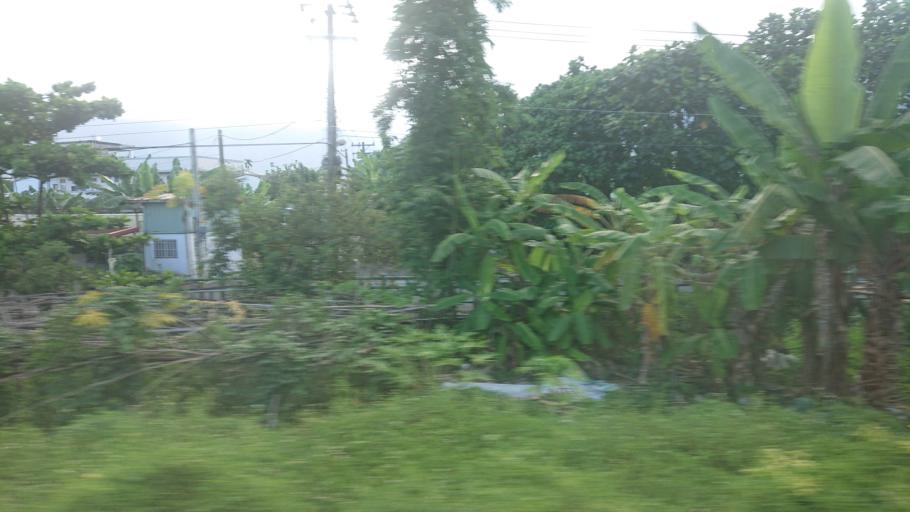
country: TW
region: Taiwan
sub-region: Hualien
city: Hualian
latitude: 23.9832
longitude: 121.5961
